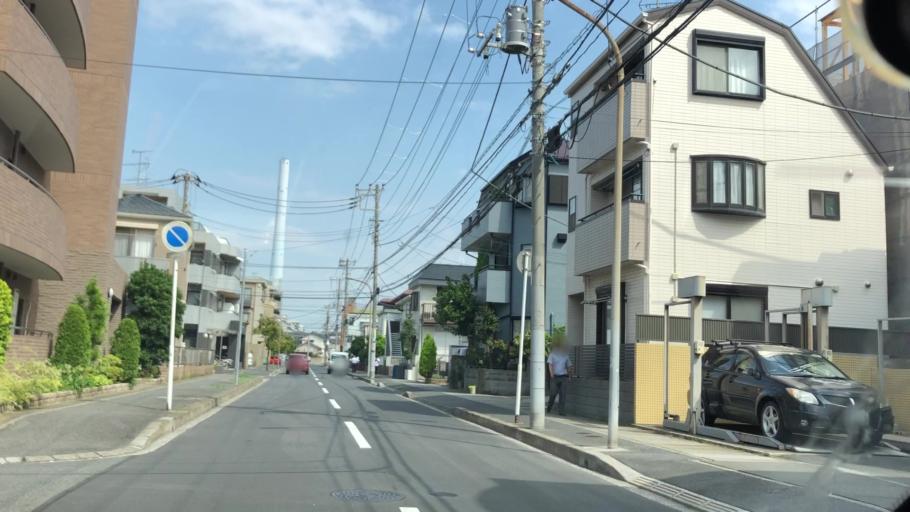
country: JP
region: Tokyo
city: Urayasu
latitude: 35.6800
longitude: 139.9095
